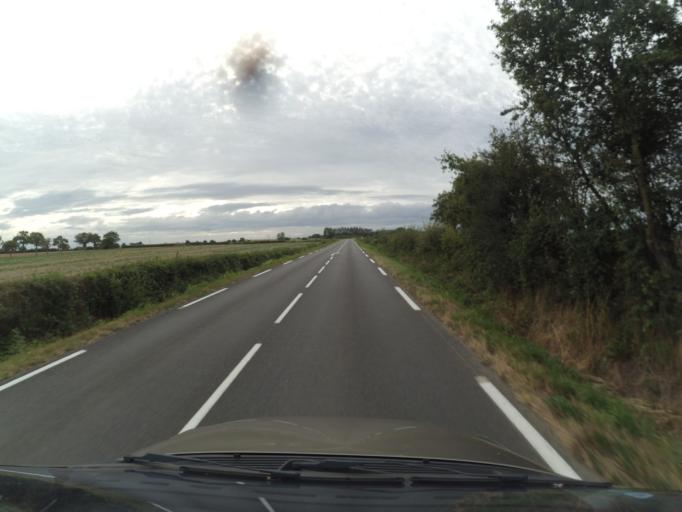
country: FR
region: Pays de la Loire
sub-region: Departement de la Vendee
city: Saint-Aubin-des-Ormeaux
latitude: 47.0180
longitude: -1.0073
